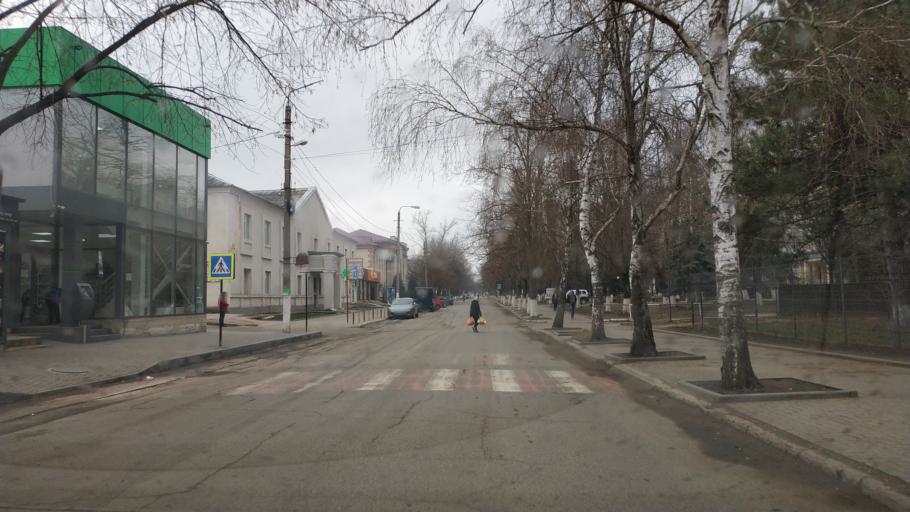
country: MD
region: Leova
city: Leova
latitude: 46.4819
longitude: 28.2518
